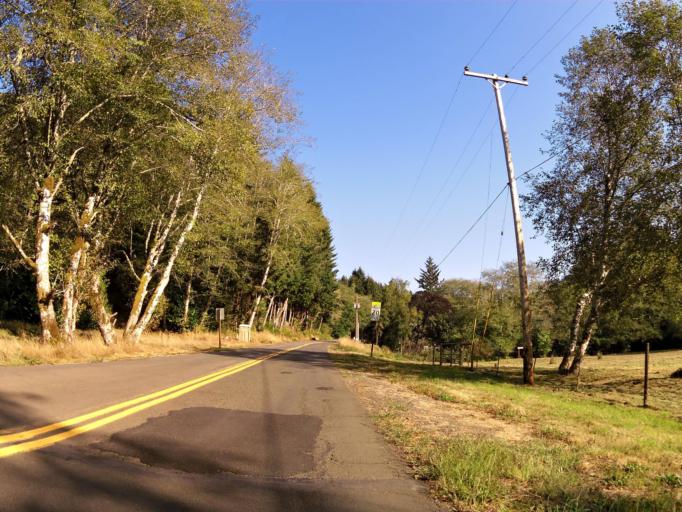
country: US
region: Oregon
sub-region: Lincoln County
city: Rose Lodge
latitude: 45.0744
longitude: -123.9264
